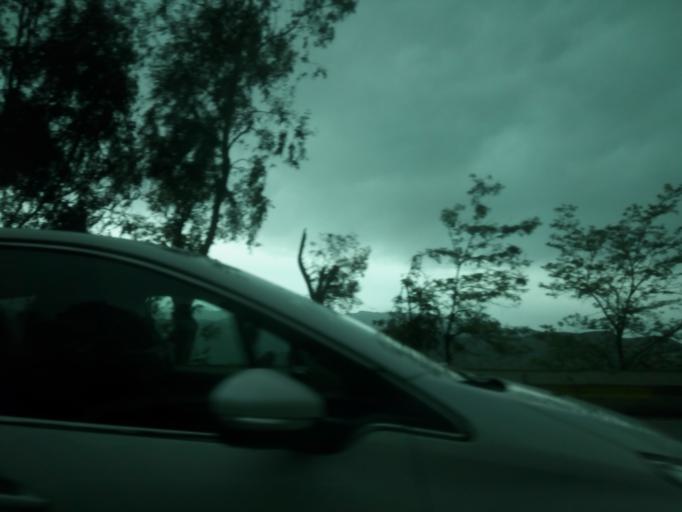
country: DZ
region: Medea
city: Medea
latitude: 36.2730
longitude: 2.7814
